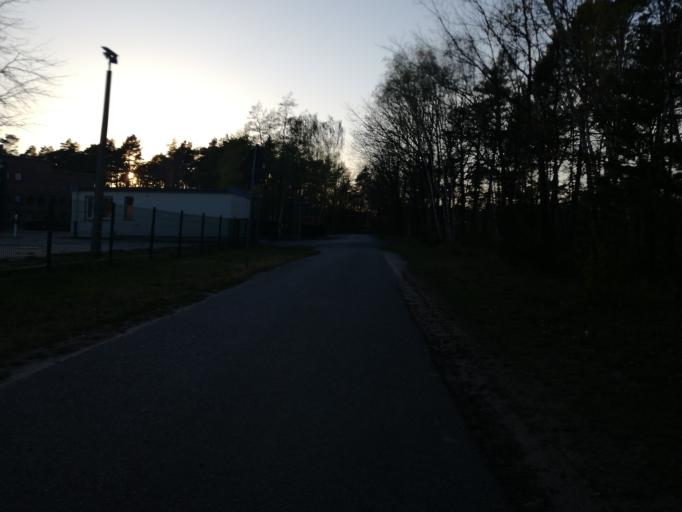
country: DE
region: Brandenburg
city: Calau
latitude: 51.7393
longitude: 13.9896
